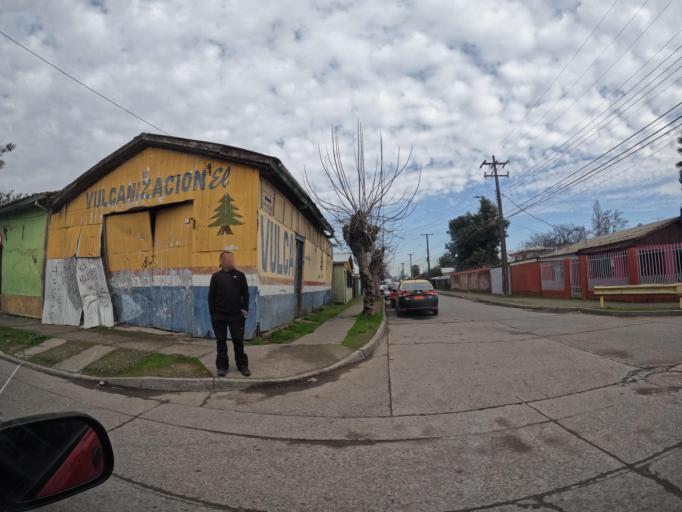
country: CL
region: Maule
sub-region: Provincia de Linares
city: Linares
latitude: -35.8579
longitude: -71.5794
